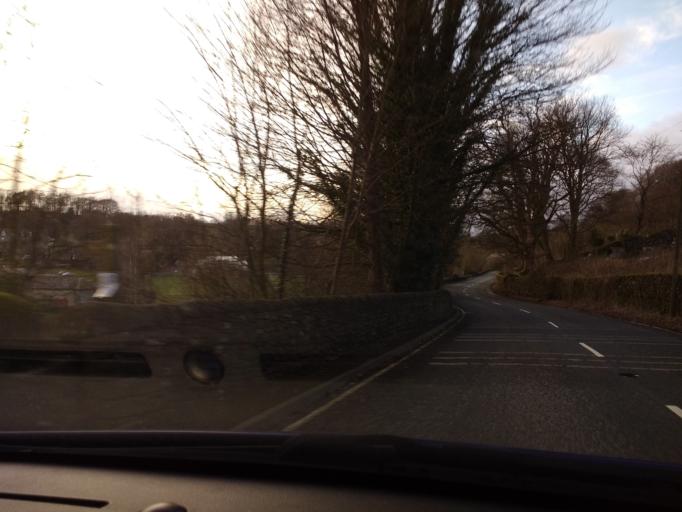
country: GB
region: England
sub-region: North Yorkshire
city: Settle
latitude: 54.0731
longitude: -2.2885
